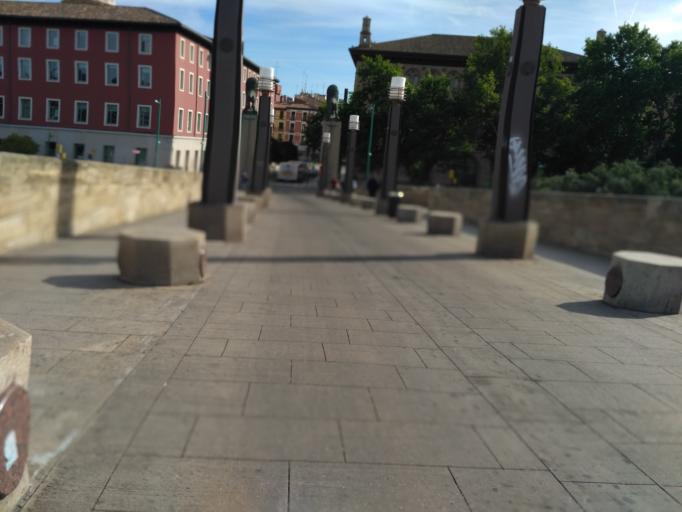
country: ES
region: Aragon
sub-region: Provincia de Zaragoza
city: Zaragoza
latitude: 41.6567
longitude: -0.8757
